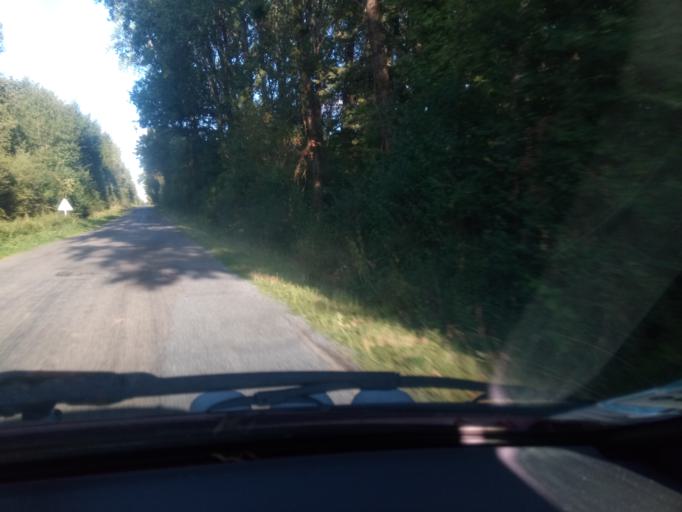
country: FR
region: Poitou-Charentes
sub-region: Departement de la Vienne
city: Availles-Limouzine
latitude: 46.1230
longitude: 0.7377
